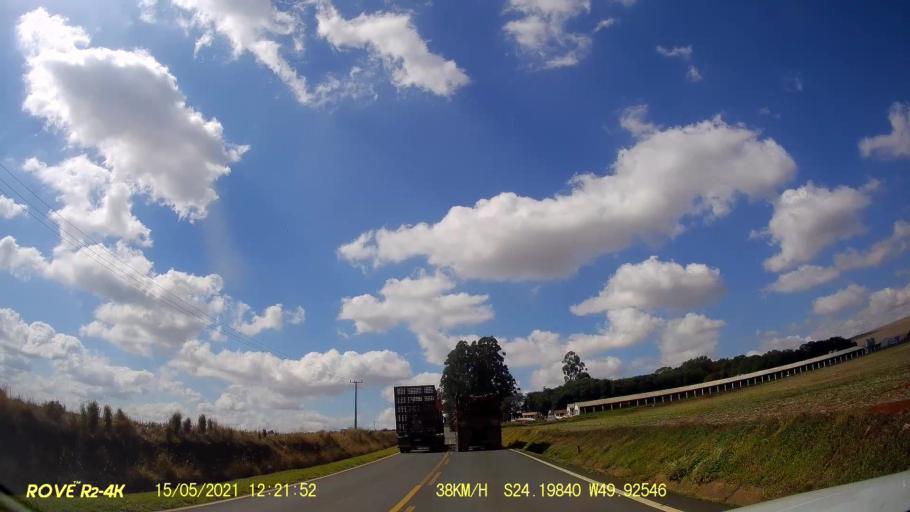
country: BR
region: Parana
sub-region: Jaguariaiva
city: Jaguariaiva
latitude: -24.1985
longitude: -49.9251
